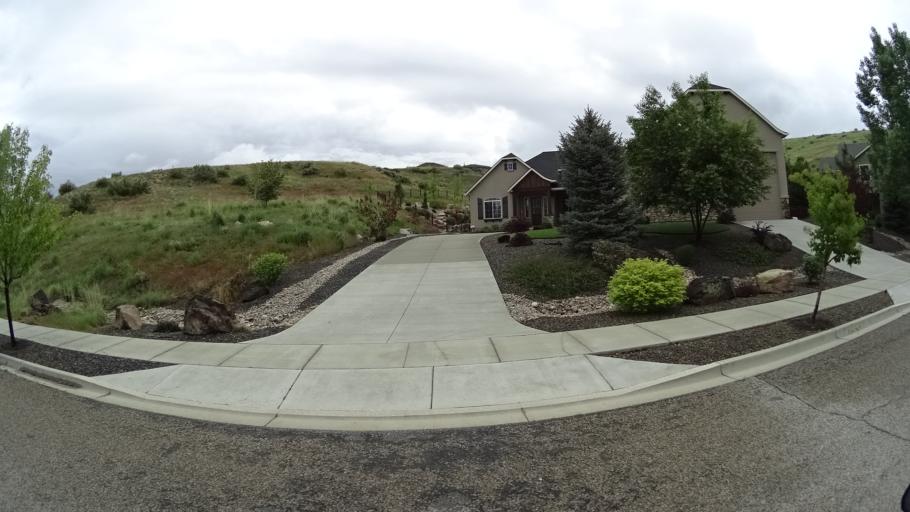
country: US
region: Idaho
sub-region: Ada County
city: Eagle
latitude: 43.7702
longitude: -116.2584
